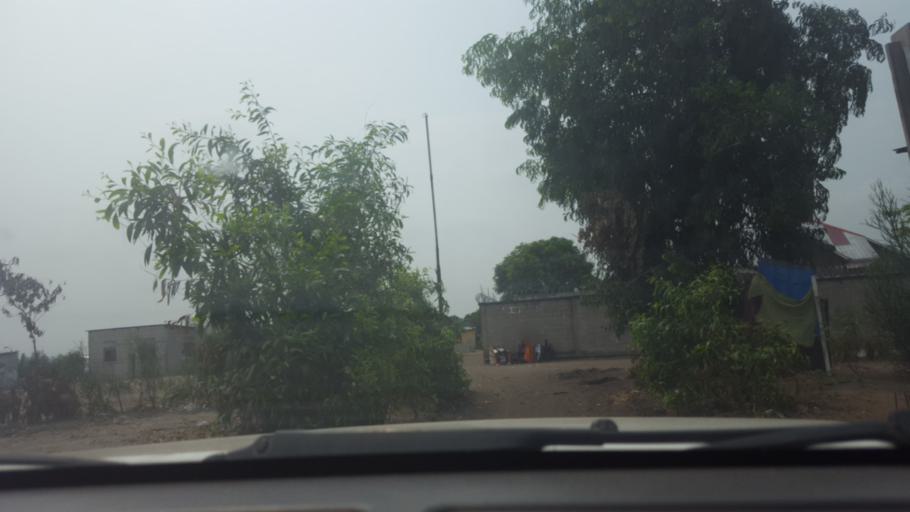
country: CD
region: Kinshasa
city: Masina
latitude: -4.3582
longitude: 15.5114
